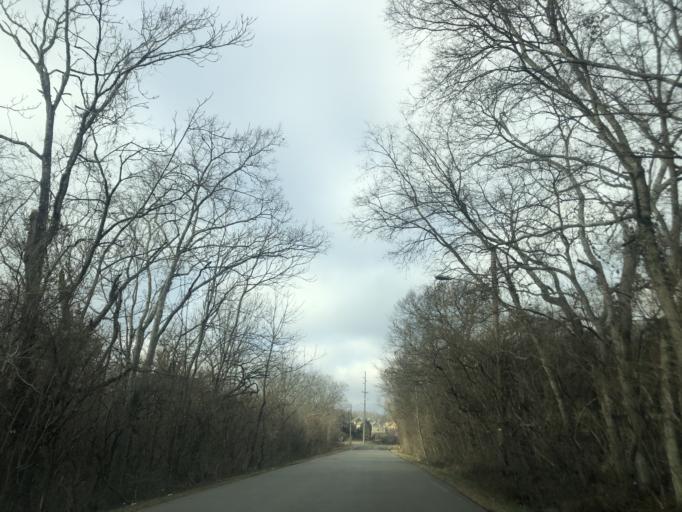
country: US
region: Tennessee
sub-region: Davidson County
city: Nashville
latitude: 36.2062
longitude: -86.7847
